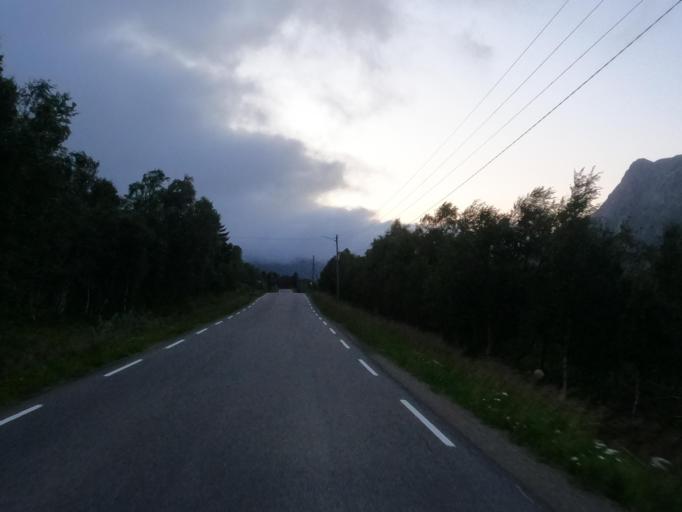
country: NO
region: Nordland
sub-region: Lodingen
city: Lodingen
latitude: 68.5810
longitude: 15.7925
